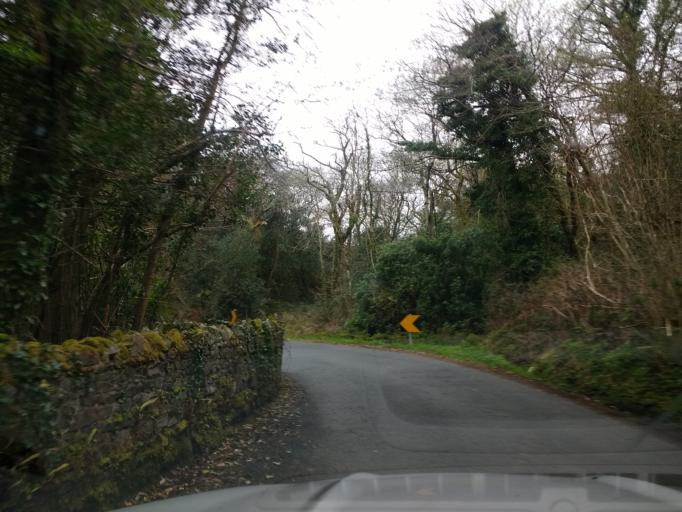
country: IE
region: Ulster
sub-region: County Donegal
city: Buncrana
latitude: 55.2170
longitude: -7.6132
